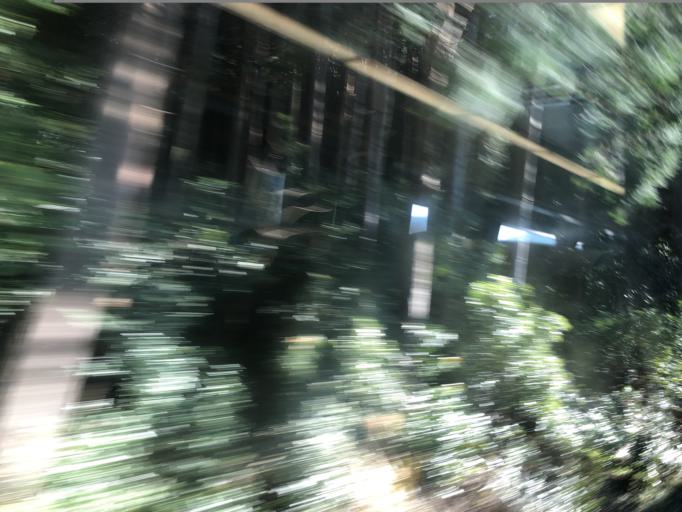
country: JP
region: Kochi
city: Nakamura
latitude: 33.0112
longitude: 132.9898
